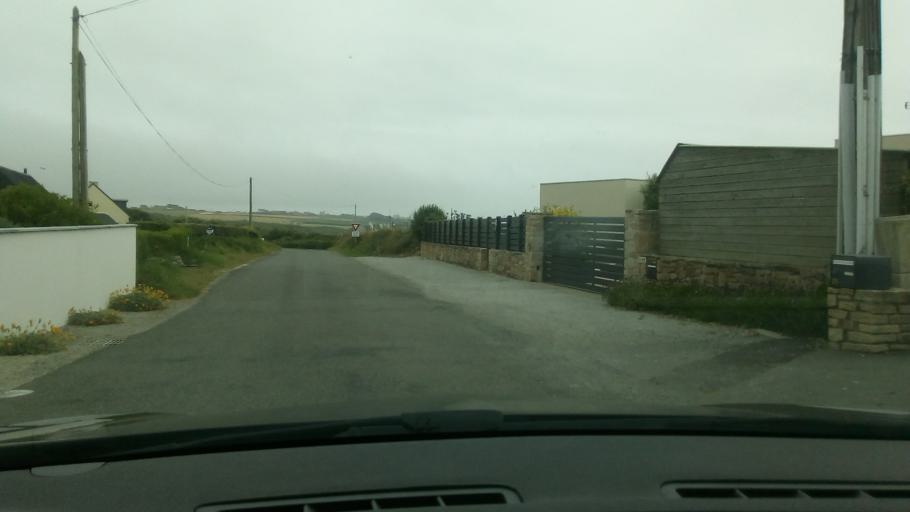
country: FR
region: Brittany
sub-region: Departement du Finistere
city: Le Conquet
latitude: 48.3508
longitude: -4.7709
